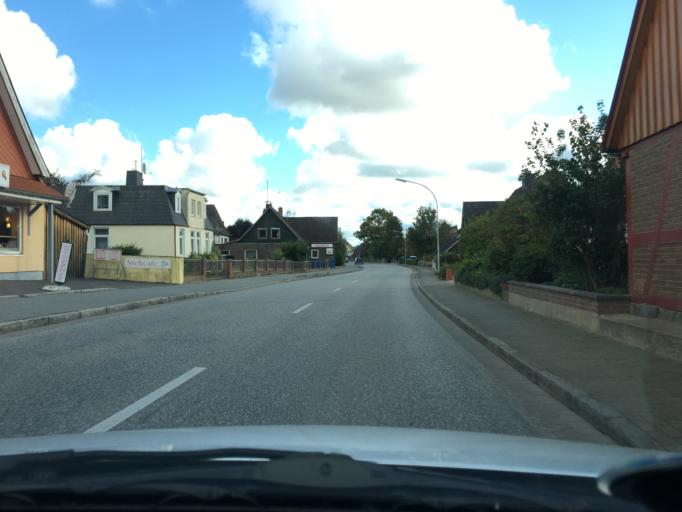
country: DE
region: Schleswig-Holstein
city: Barsbek
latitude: 54.4042
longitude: 10.3226
